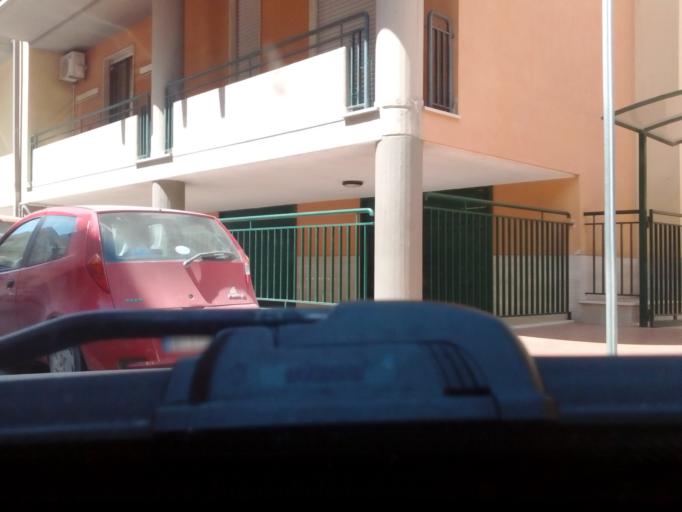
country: IT
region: Apulia
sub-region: Provincia di Bari
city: Gravina in Puglia
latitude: 40.8206
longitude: 16.4277
